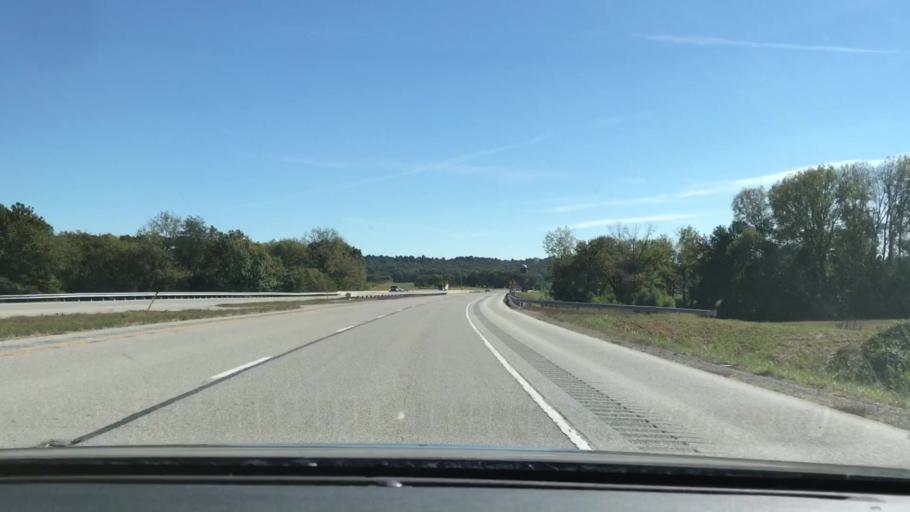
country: US
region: Kentucky
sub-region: Todd County
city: Elkton
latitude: 36.8246
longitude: -87.1569
